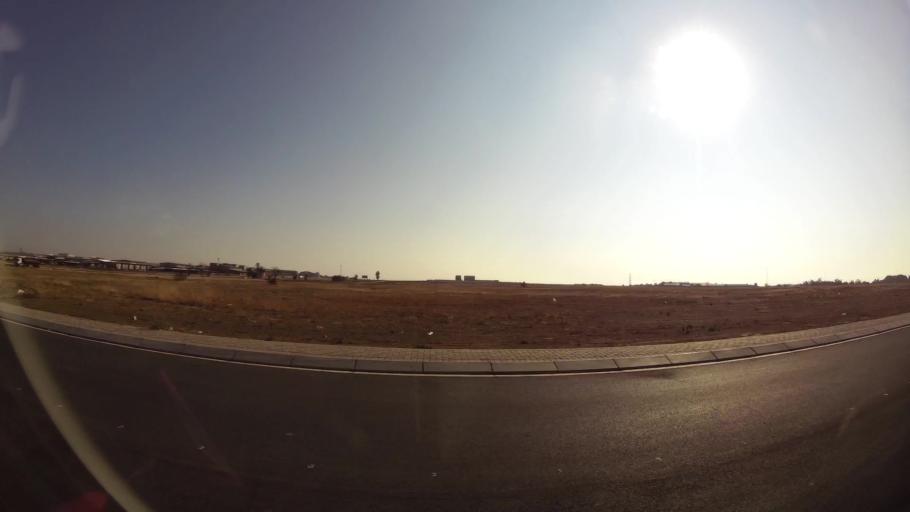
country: ZA
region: Orange Free State
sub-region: Mangaung Metropolitan Municipality
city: Bloemfontein
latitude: -29.1930
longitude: 26.2164
